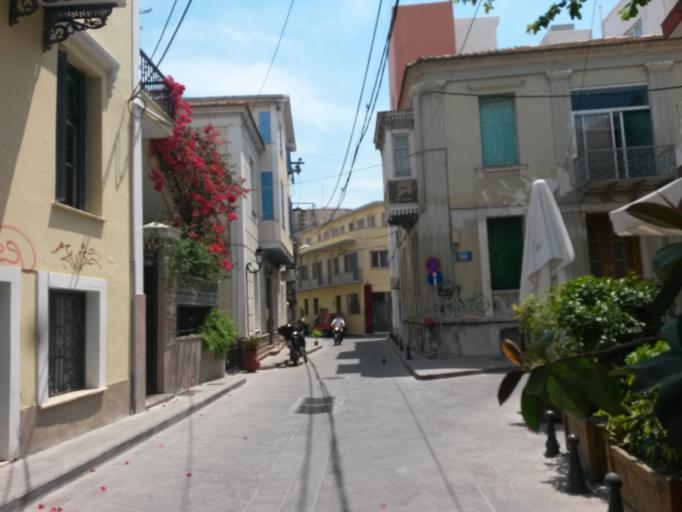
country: GR
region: North Aegean
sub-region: Nomos Lesvou
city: Mytilini
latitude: 39.1061
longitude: 26.5591
